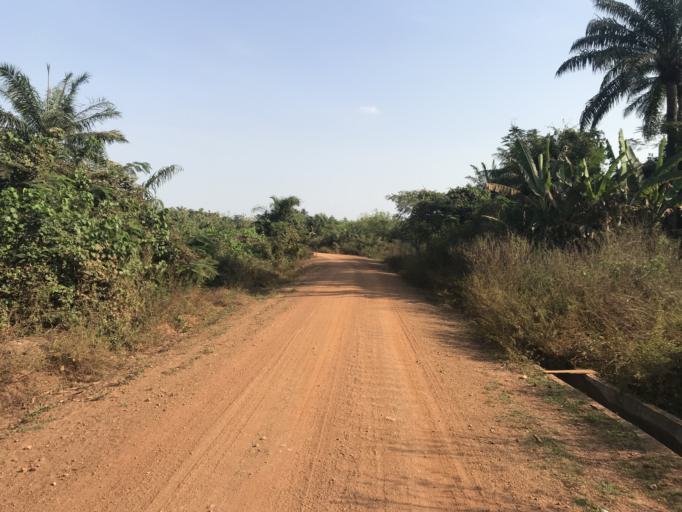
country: NG
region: Osun
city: Inisa
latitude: 7.7995
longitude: 4.2855
